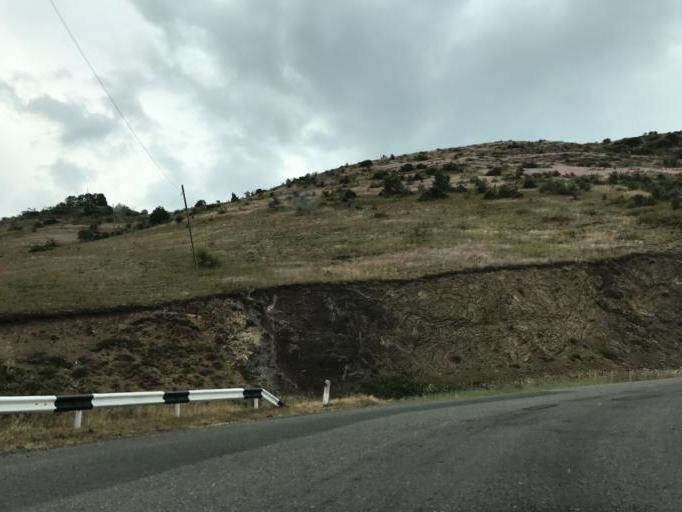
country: AZ
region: Lacin
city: Lacin
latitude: 39.6841
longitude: 46.6343
